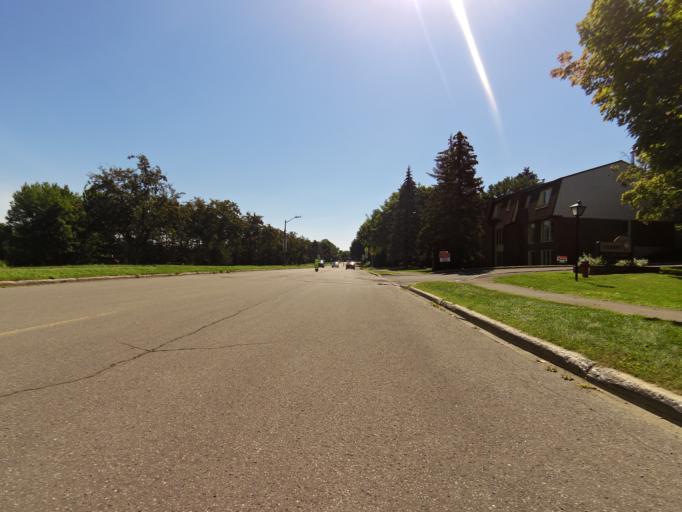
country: CA
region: Ontario
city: Ottawa
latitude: 45.3542
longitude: -75.6662
